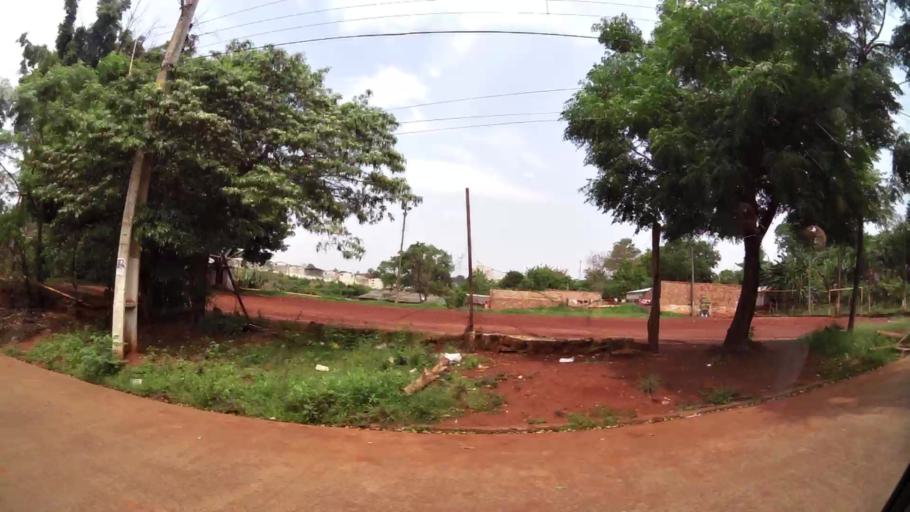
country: PY
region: Alto Parana
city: Ciudad del Este
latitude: -25.5034
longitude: -54.6188
